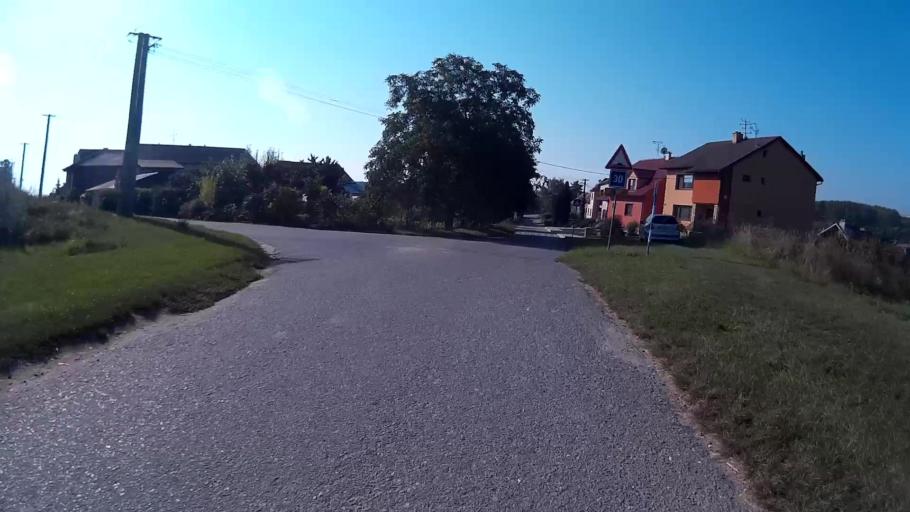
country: CZ
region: South Moravian
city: Vranovice
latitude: 48.9333
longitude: 16.5762
